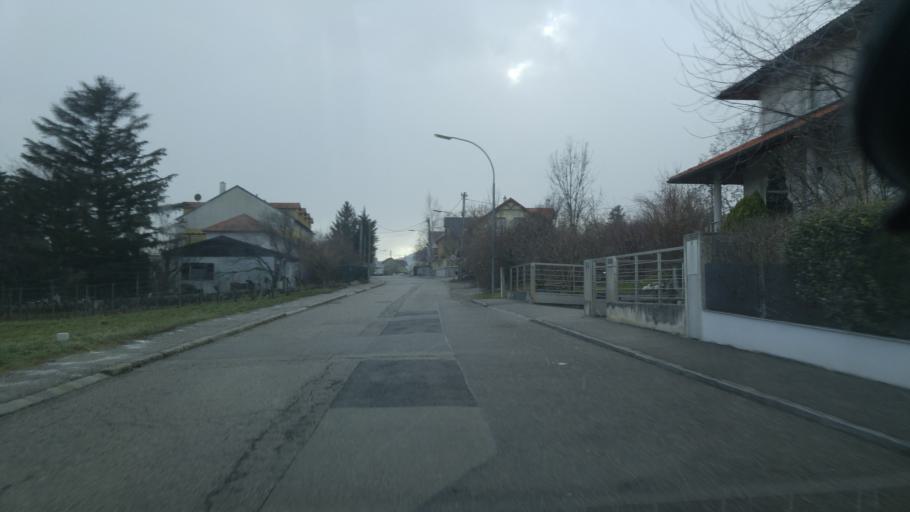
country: AT
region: Lower Austria
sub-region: Politischer Bezirk Baden
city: Baden
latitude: 47.9965
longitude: 16.2103
